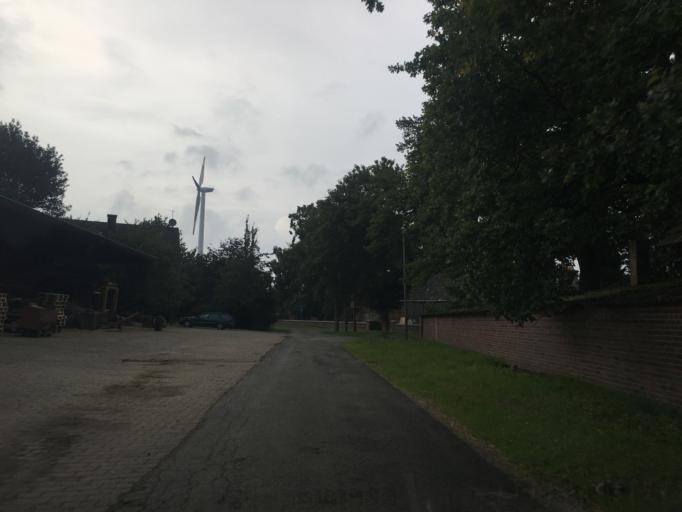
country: DE
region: North Rhine-Westphalia
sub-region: Regierungsbezirk Munster
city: Greven
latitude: 52.0506
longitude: 7.6043
